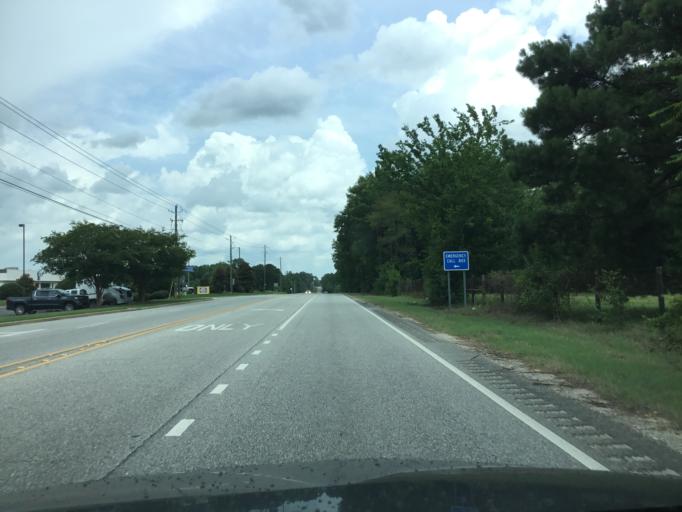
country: US
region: Alabama
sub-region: Montgomery County
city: Pike Road
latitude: 32.3468
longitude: -86.0913
